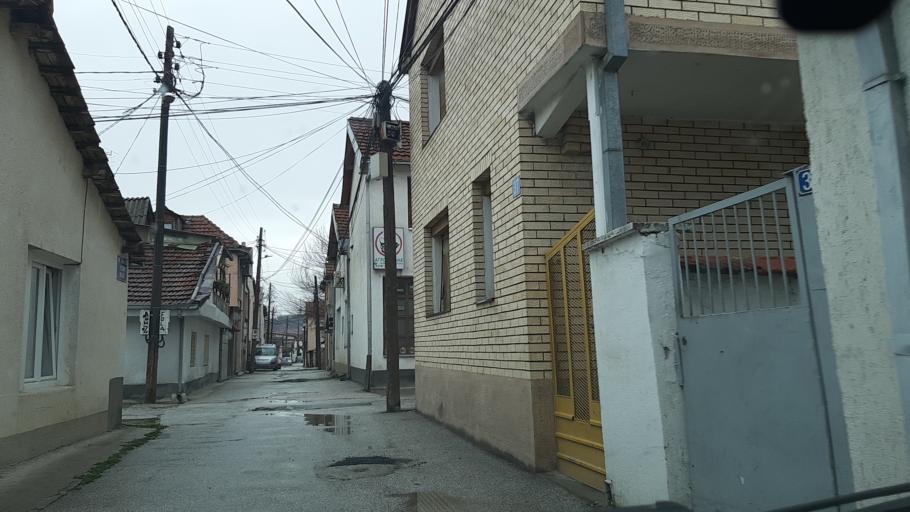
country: MK
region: Karpos
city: Skopje
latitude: 41.9937
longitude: 21.4458
